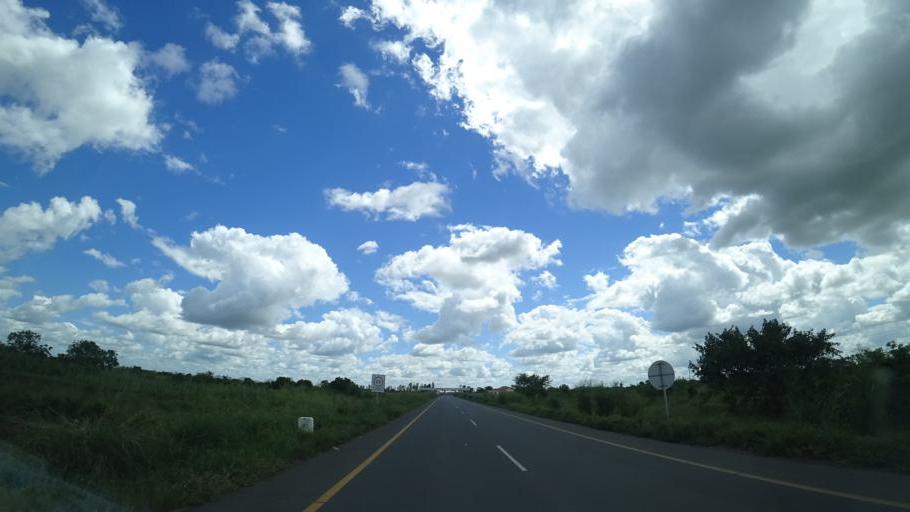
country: MZ
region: Sofala
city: Dondo
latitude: -19.2890
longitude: 34.2293
